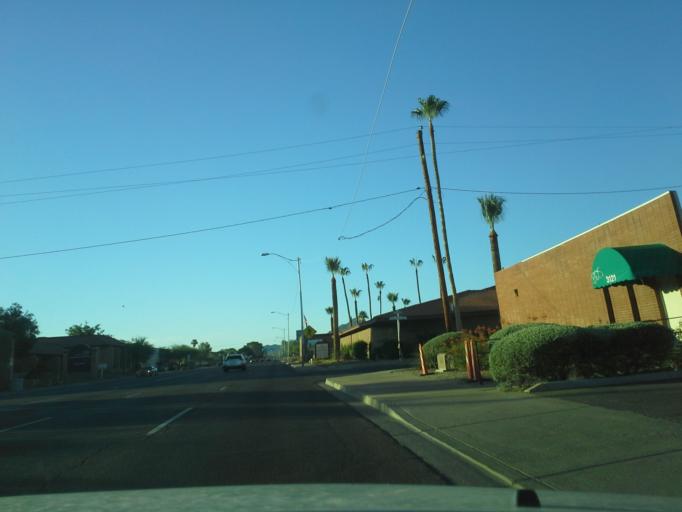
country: US
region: Arizona
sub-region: Maricopa County
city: Phoenix
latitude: 33.4845
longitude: -112.0301
